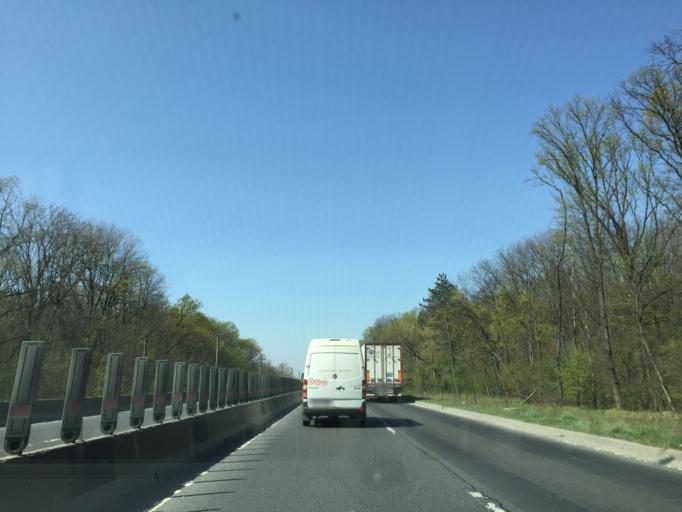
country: RO
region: Ilfov
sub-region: Comuna Tunari
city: Tunari
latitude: 44.5394
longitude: 26.1084
